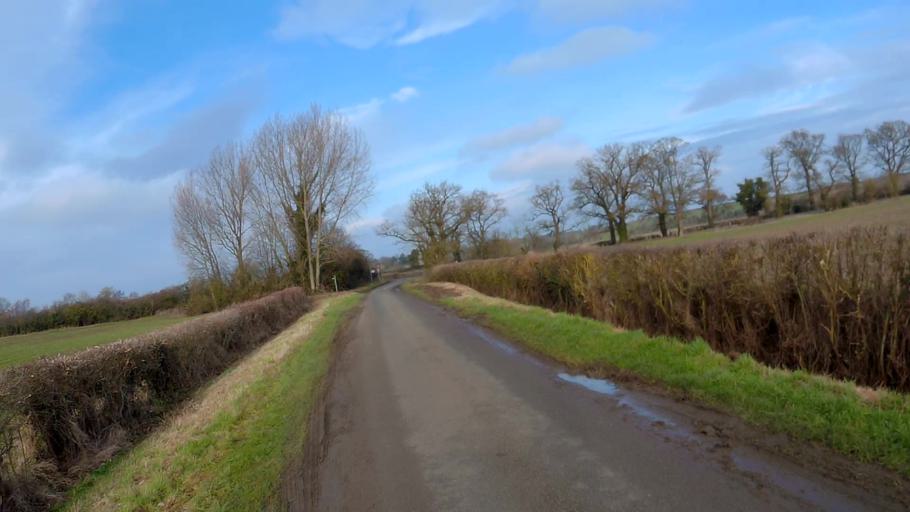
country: GB
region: England
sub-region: Lincolnshire
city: Bourne
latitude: 52.7757
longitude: -0.4261
